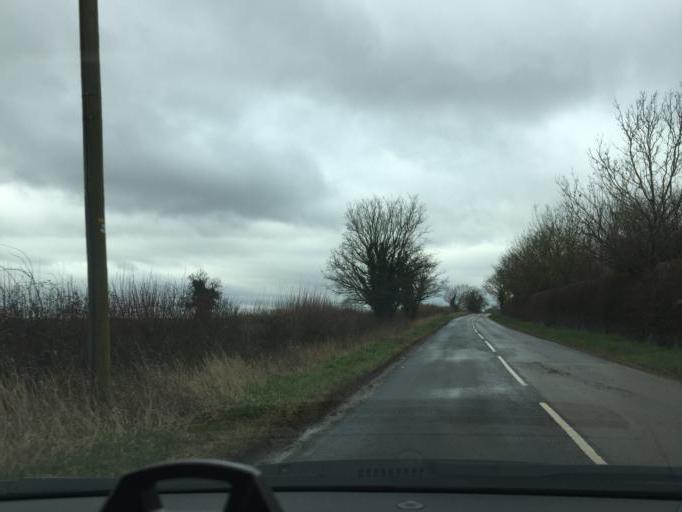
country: GB
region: England
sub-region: Northamptonshire
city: Brackley
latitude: 52.0940
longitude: -1.1277
